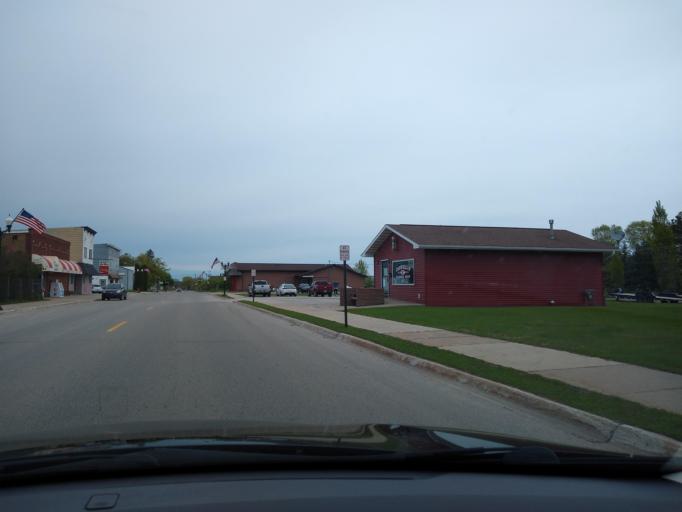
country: US
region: Michigan
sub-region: Delta County
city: Escanaba
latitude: 45.7649
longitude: -87.0691
